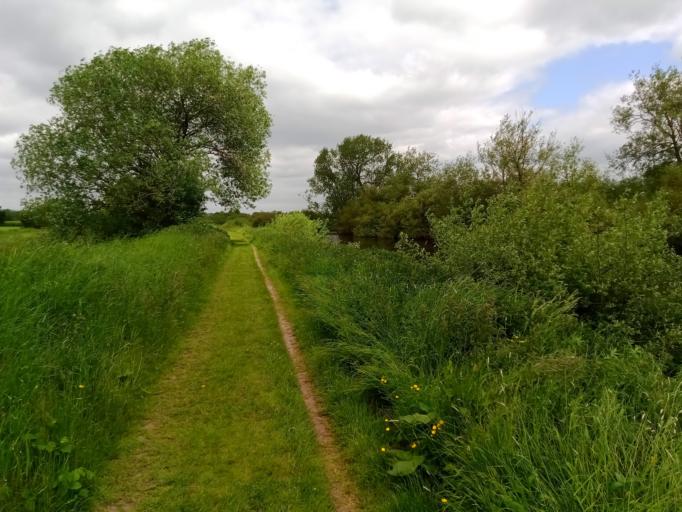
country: IE
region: Leinster
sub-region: County Carlow
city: Bagenalstown
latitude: 52.7594
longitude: -6.9600
